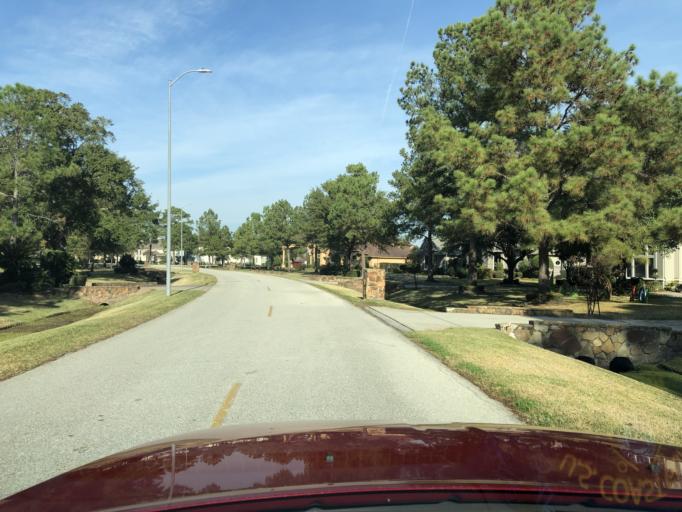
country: US
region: Texas
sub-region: Harris County
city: Tomball
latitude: 30.0418
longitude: -95.5578
